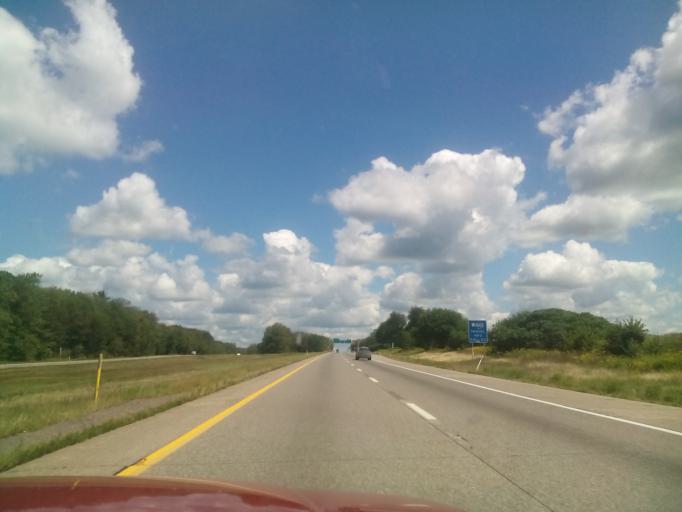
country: US
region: Pennsylvania
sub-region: Luzerne County
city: Conyngham
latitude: 41.0431
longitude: -76.0254
